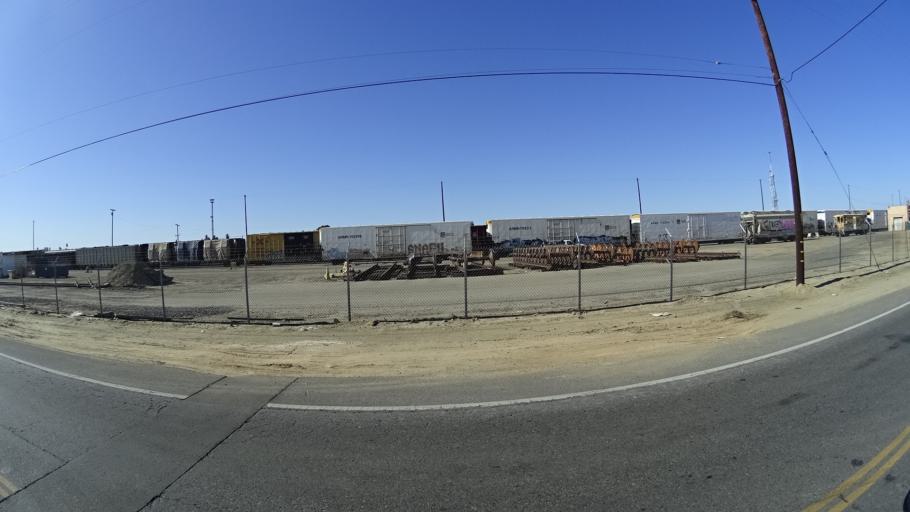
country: US
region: California
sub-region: Fresno County
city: West Park
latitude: 36.7841
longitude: -119.8472
